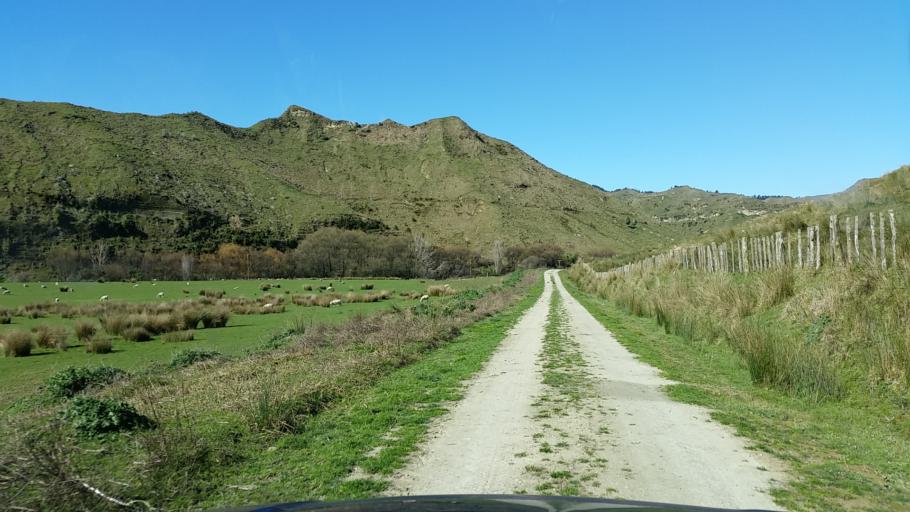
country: NZ
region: Manawatu-Wanganui
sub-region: Wanganui District
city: Wanganui
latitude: -39.6700
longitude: 174.8581
